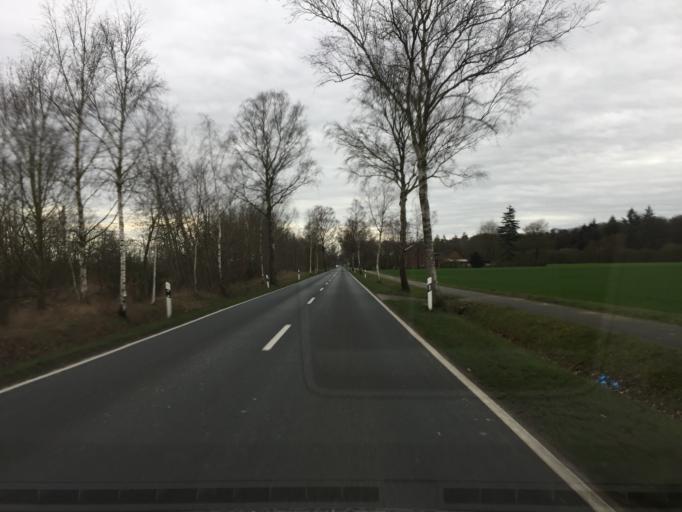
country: DE
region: Lower Saxony
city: Schwaforden
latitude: 52.7319
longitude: 8.8167
